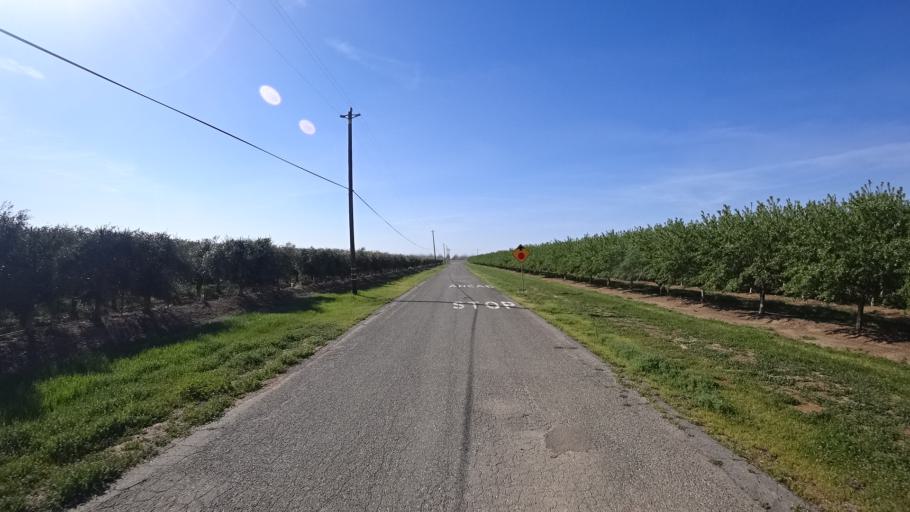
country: US
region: California
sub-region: Glenn County
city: Willows
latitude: 39.6270
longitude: -122.2160
